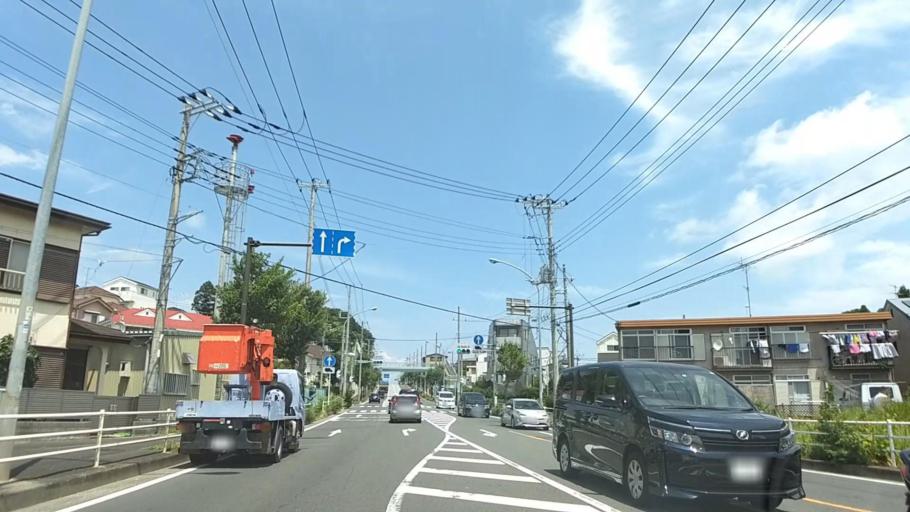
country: JP
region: Kanagawa
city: Minami-rinkan
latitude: 35.4529
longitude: 139.4826
